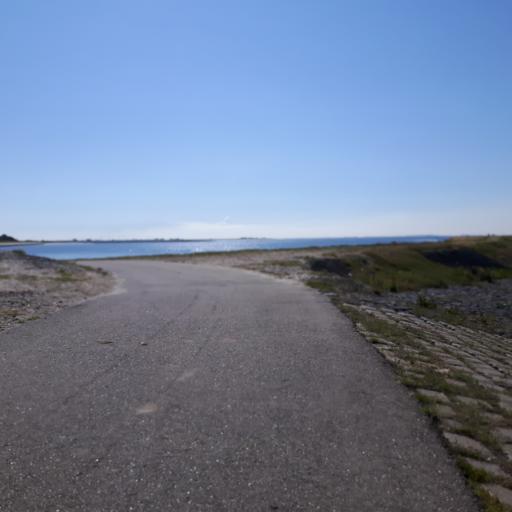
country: NL
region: Zeeland
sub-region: Gemeente Goes
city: Goes
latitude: 51.6254
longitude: 3.9465
